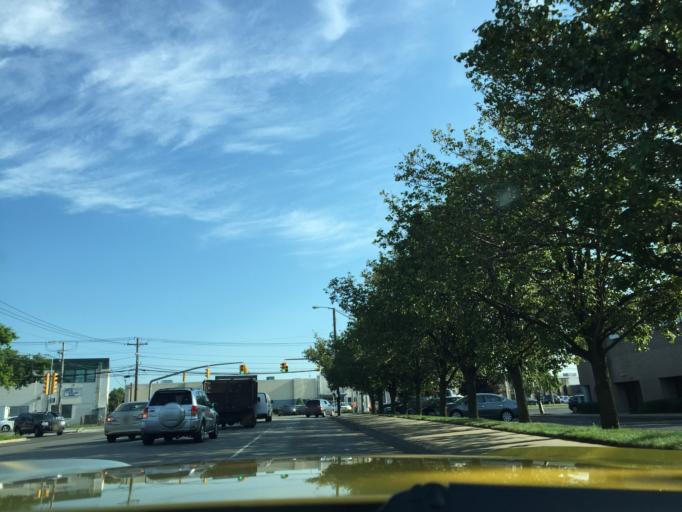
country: US
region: New York
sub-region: Nassau County
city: New Cassel
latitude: 40.7647
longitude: -73.5480
